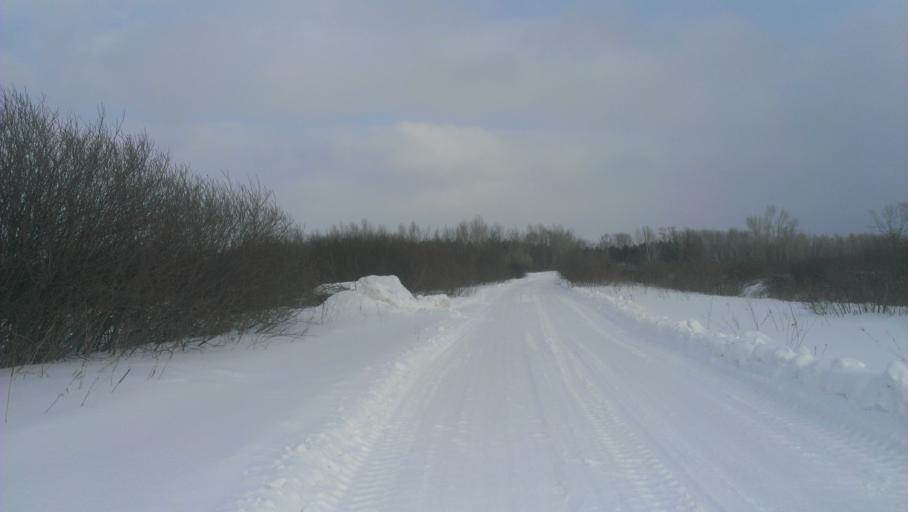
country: RU
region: Altai Krai
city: Zaton
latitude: 53.3123
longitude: 83.8362
